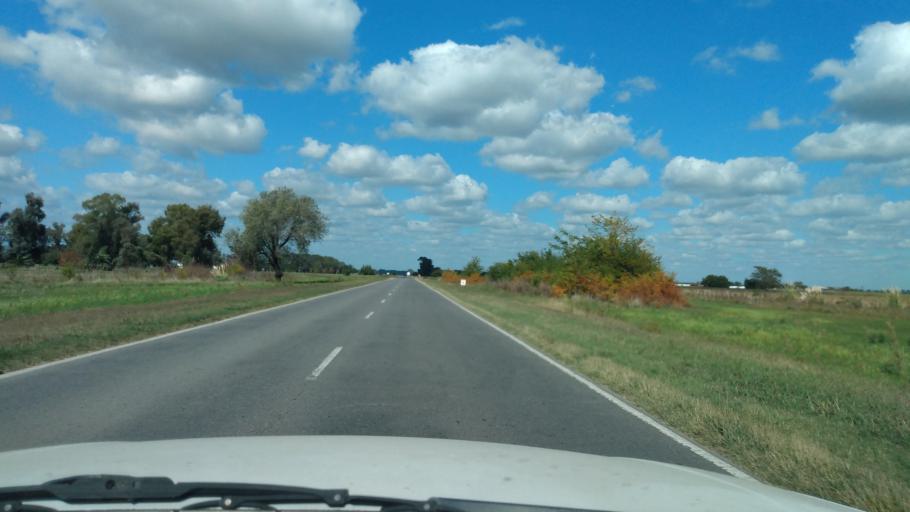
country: AR
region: Buenos Aires
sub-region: Partido de Navarro
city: Navarro
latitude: -34.9505
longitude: -59.3200
